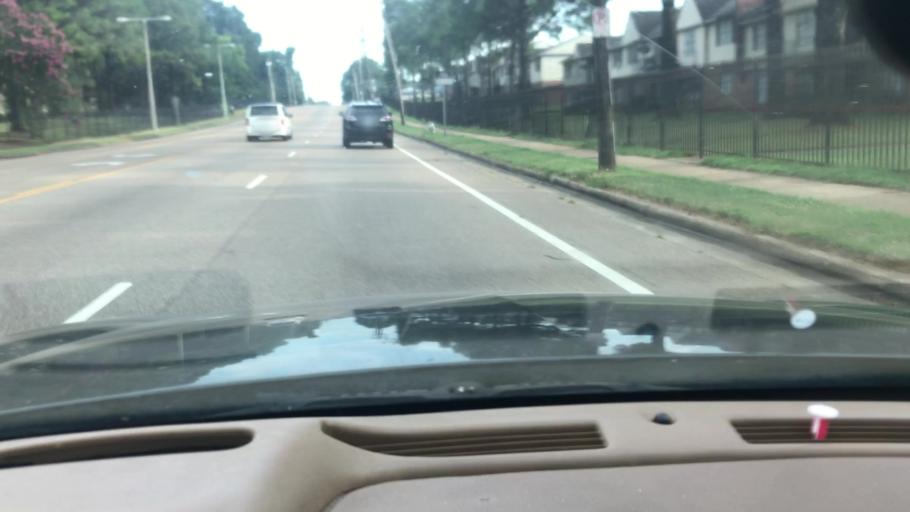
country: US
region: Tennessee
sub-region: Shelby County
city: New South Memphis
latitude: 35.0513
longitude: -90.0075
